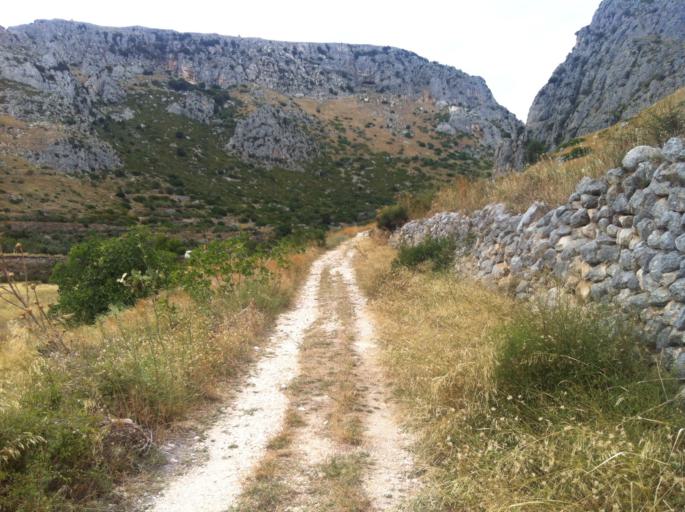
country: IT
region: Apulia
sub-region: Provincia di Foggia
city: Manfredonia
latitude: 41.6662
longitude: 15.9110
